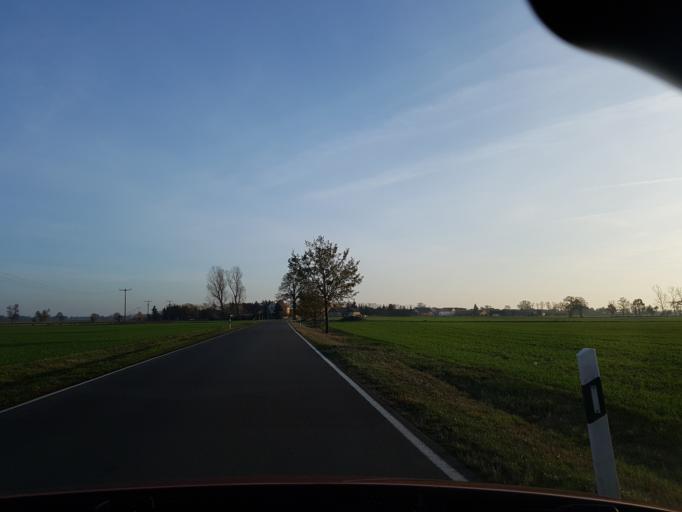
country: DE
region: Saxony
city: Nauwalde
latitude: 51.4667
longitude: 13.4286
